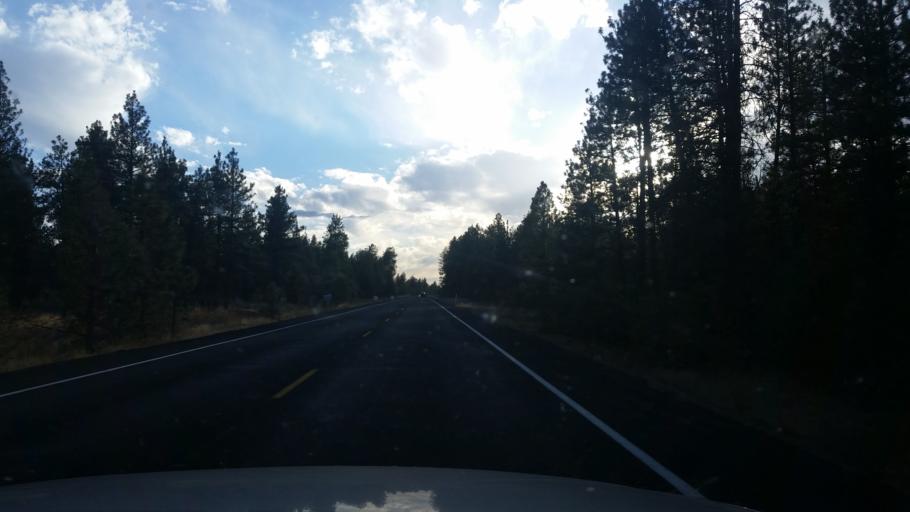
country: US
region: Washington
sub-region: Spokane County
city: Medical Lake
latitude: 47.4552
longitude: -117.6990
